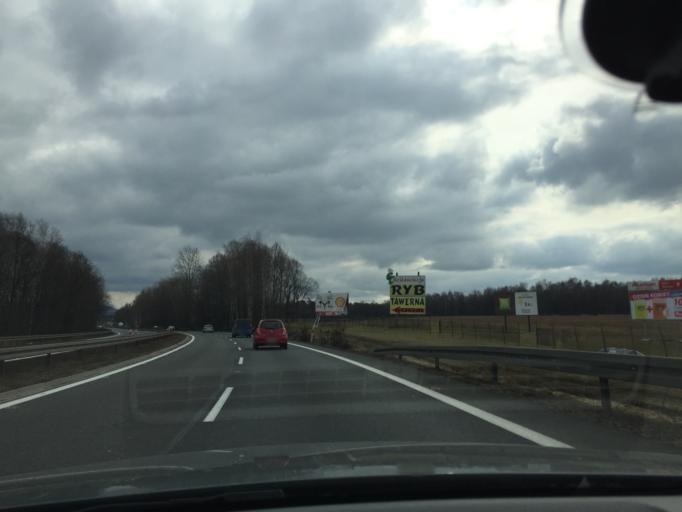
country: PL
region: Silesian Voivodeship
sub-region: Powiat bielski
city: Mazancowice
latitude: 49.8777
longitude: 18.9980
